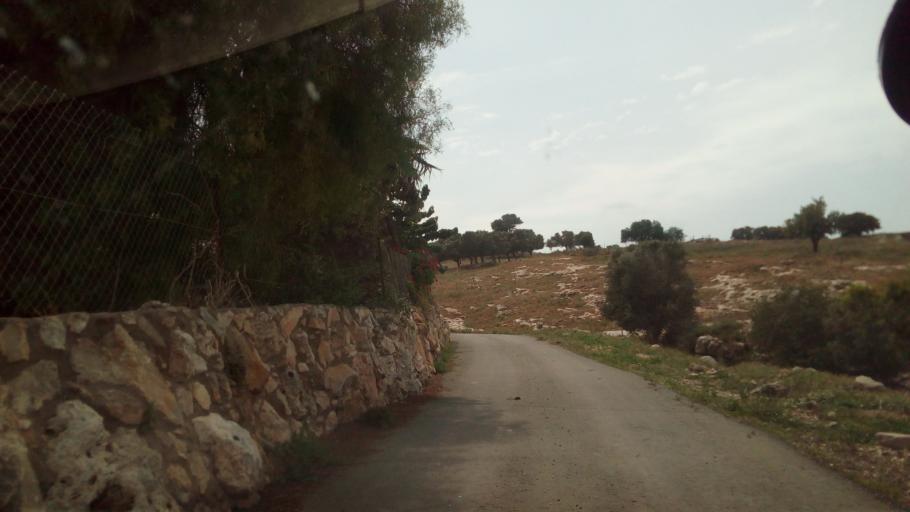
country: CY
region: Pafos
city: Polis
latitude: 34.9988
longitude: 32.3785
